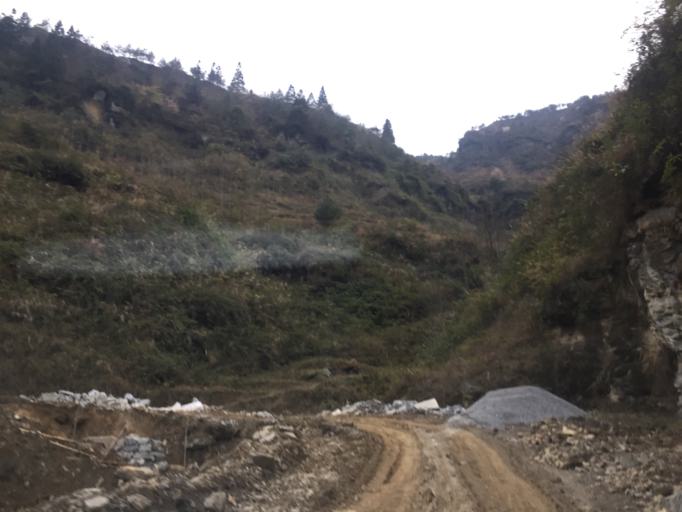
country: CN
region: Guizhou Sheng
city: Changfeng
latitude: 28.4788
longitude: 108.0745
